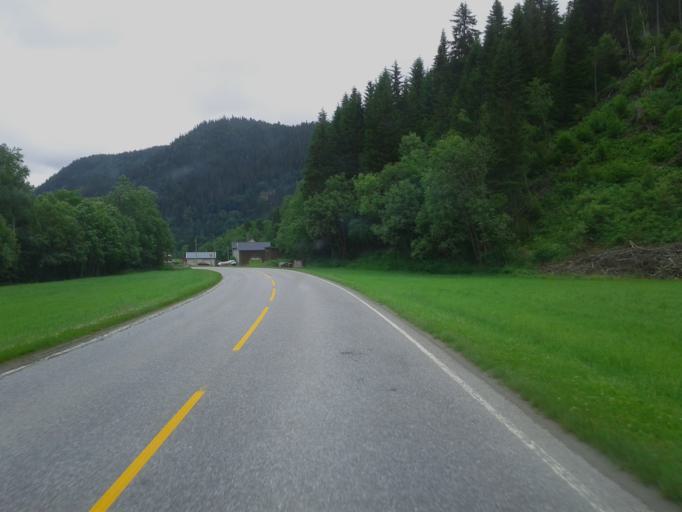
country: NO
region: Sor-Trondelag
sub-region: Midtre Gauldal
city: Storen
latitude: 63.0147
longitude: 10.3508
